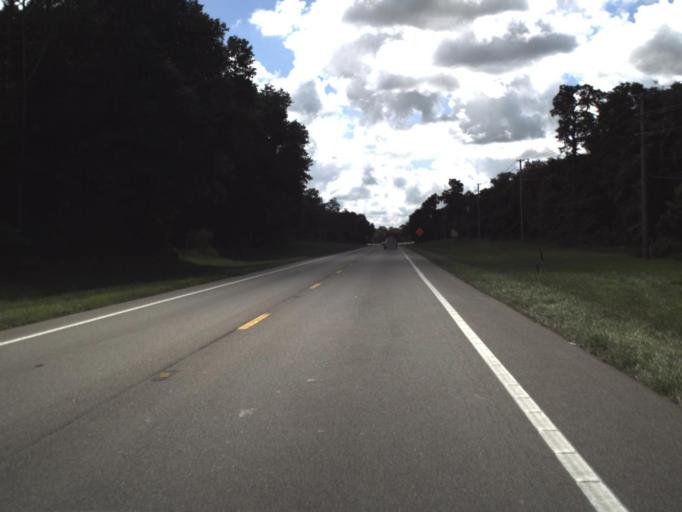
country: US
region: Florida
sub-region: Polk County
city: Gibsonia
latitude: 28.1717
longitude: -81.9822
